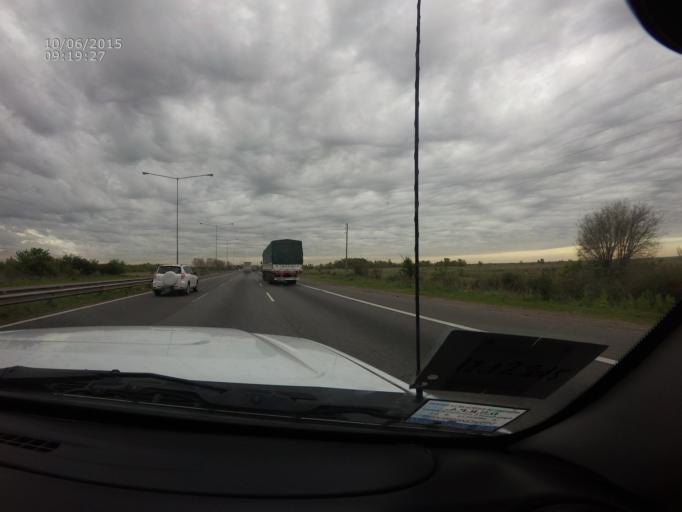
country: AR
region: Buenos Aires
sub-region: Partido de Campana
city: Campana
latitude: -34.2665
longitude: -58.8999
